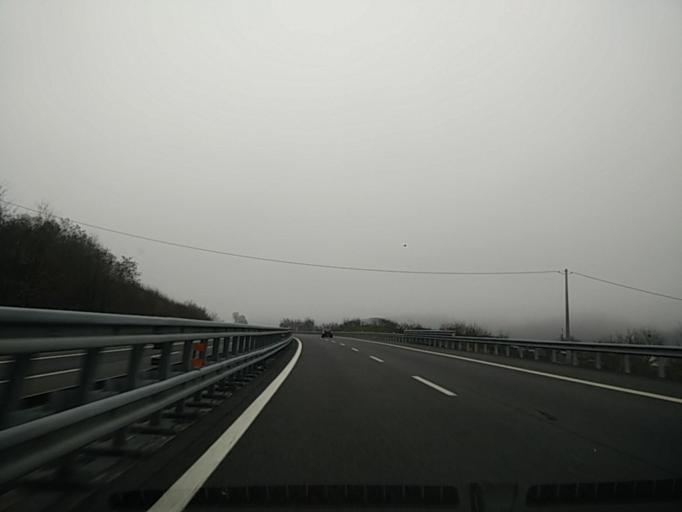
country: IT
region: Piedmont
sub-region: Provincia di Asti
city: Tigliole
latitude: 44.9031
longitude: 8.0598
